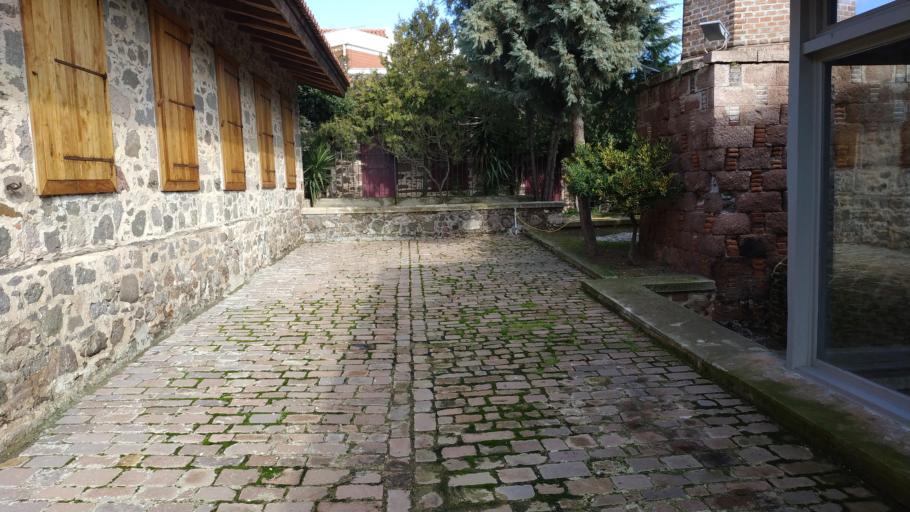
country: GR
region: North Aegean
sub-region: Nomos Lesvou
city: Agia Paraskevi
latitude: 39.2445
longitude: 26.2684
